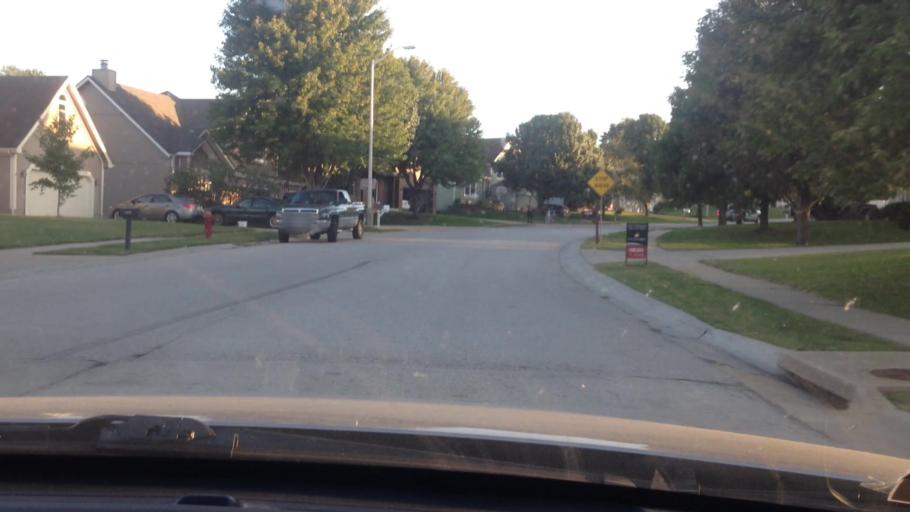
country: US
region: Missouri
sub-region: Clay County
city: Smithville
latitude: 39.3022
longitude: -94.5902
